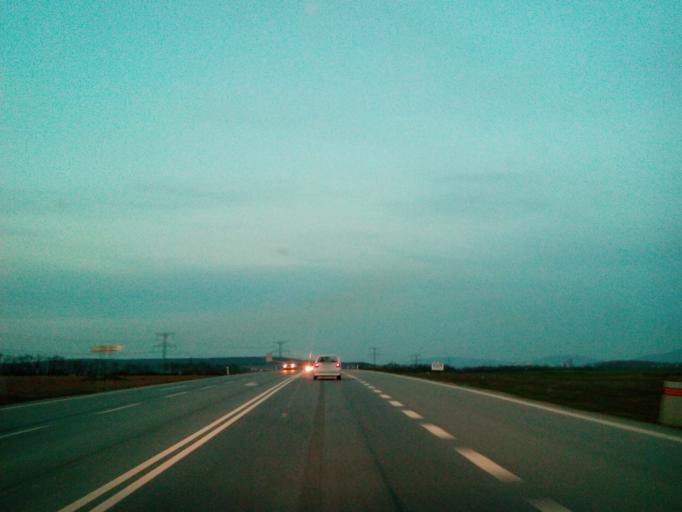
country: SK
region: Kosicky
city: Moldava nad Bodvou
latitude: 48.6181
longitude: 21.1403
